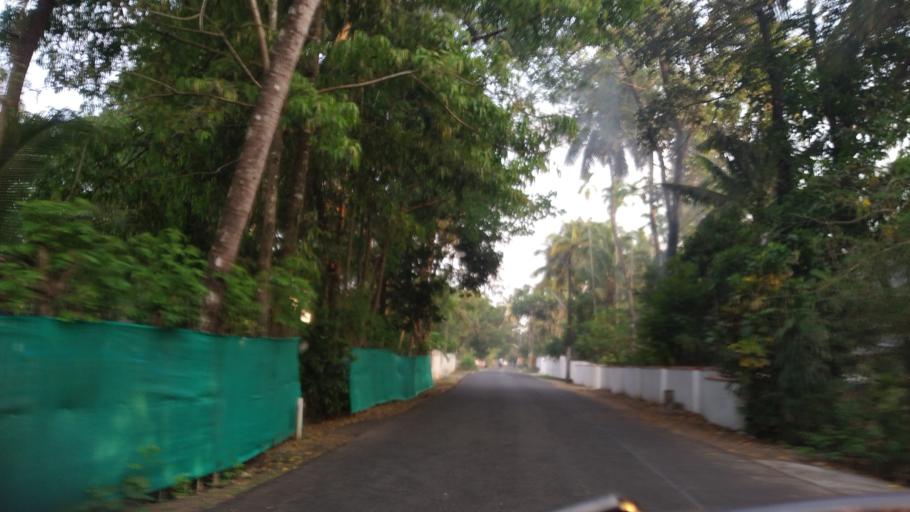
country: IN
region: Kerala
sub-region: Thrissur District
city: Thanniyam
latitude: 10.3645
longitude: 76.1073
